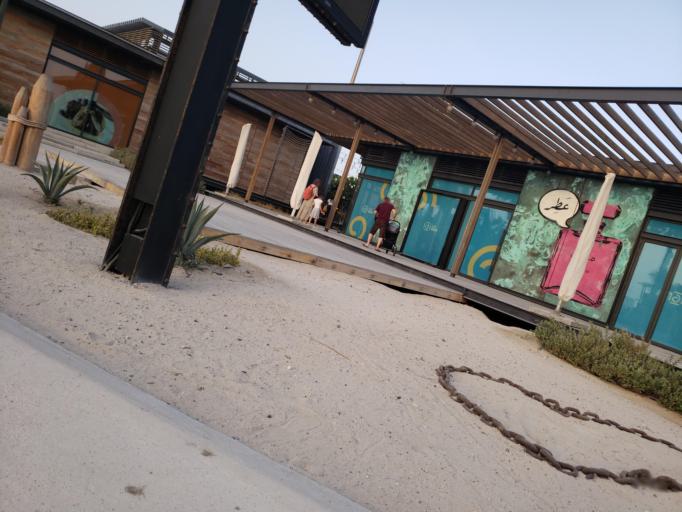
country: AE
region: Dubai
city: Dubai
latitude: 25.2279
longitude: 55.2572
